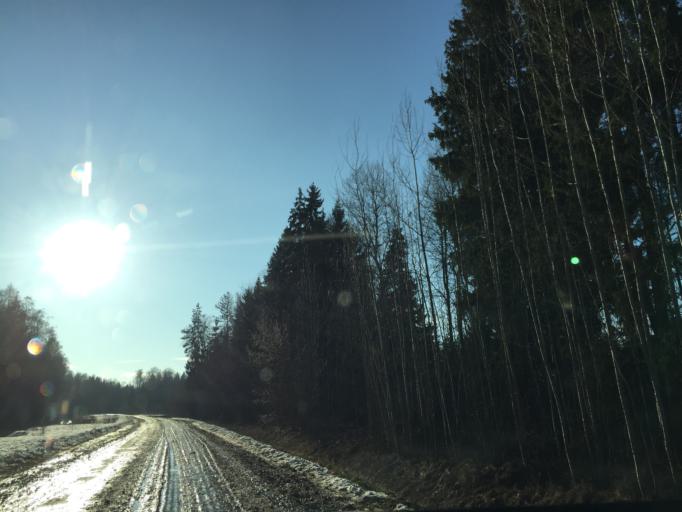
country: LV
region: Lecava
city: Iecava
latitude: 56.6889
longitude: 24.0759
